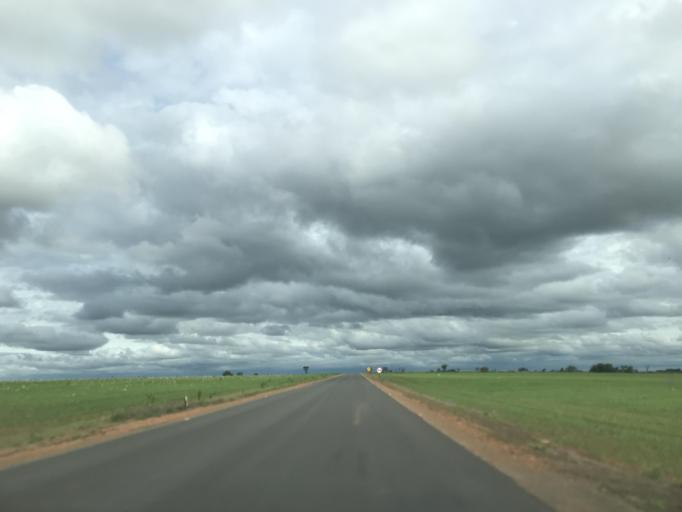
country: BR
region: Goias
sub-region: Vianopolis
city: Vianopolis
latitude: -16.9641
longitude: -48.6201
